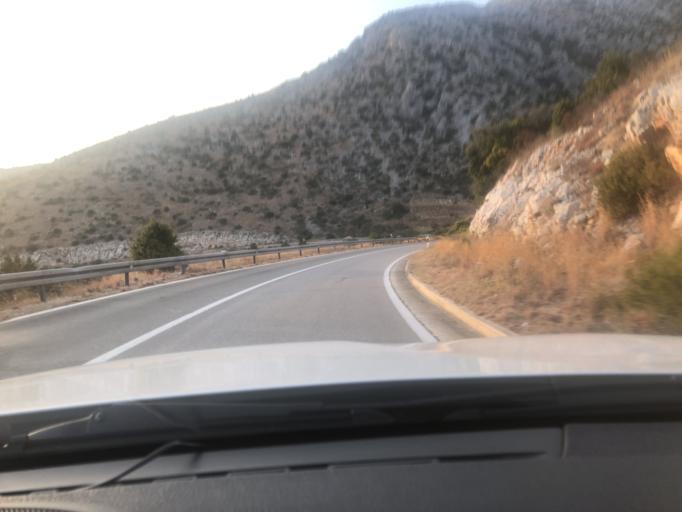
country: HR
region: Splitsko-Dalmatinska
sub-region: Grad Hvar
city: Hvar
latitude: 43.1562
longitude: 16.5082
